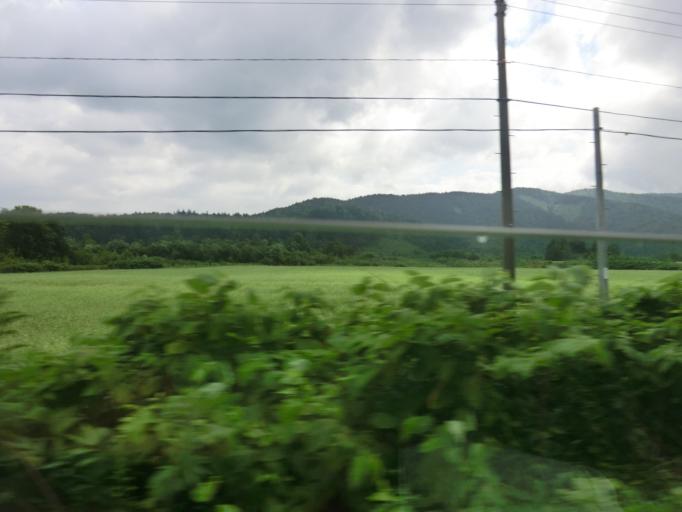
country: JP
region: Hokkaido
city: Nayoro
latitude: 44.1668
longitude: 142.1483
